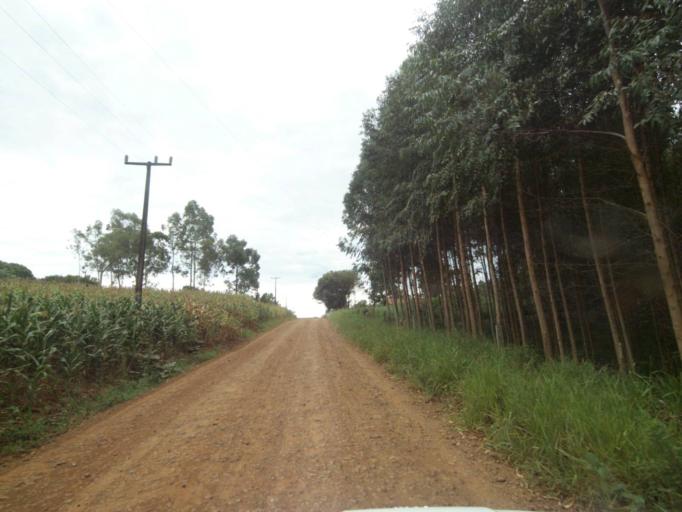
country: BR
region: Parana
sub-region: Guaraniacu
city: Guaraniacu
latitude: -24.9111
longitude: -52.9358
